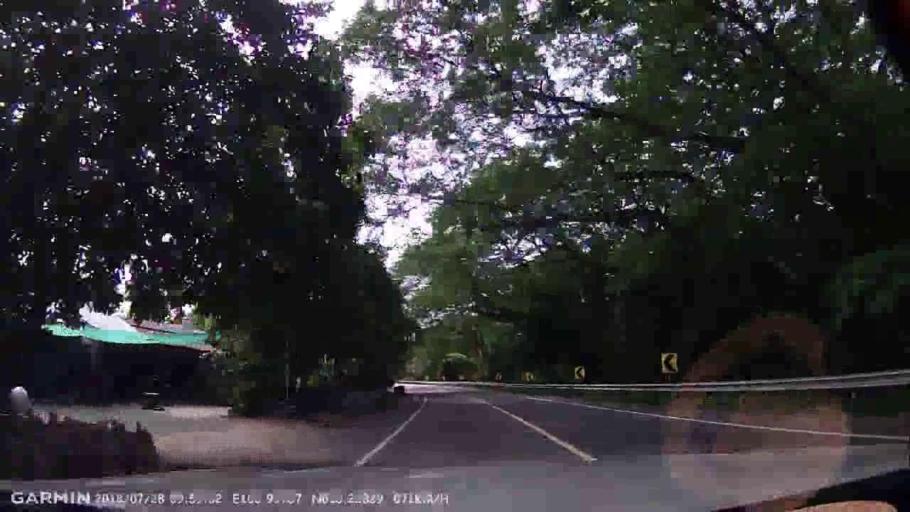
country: TH
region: Chon Buri
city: Si Racha
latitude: 13.2282
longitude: 100.9975
